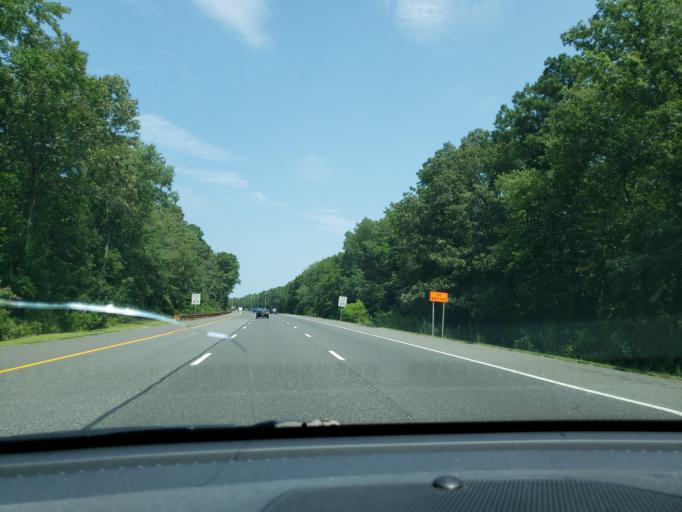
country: US
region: New Jersey
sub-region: Atlantic County
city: Northfield
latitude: 39.3875
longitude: -74.5706
